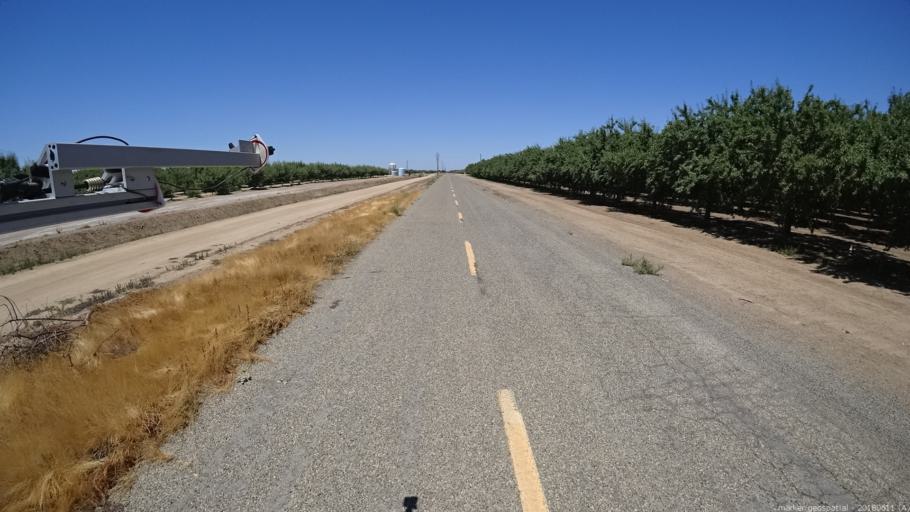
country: US
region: California
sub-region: Madera County
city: Fairmead
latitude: 37.0310
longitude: -120.2115
